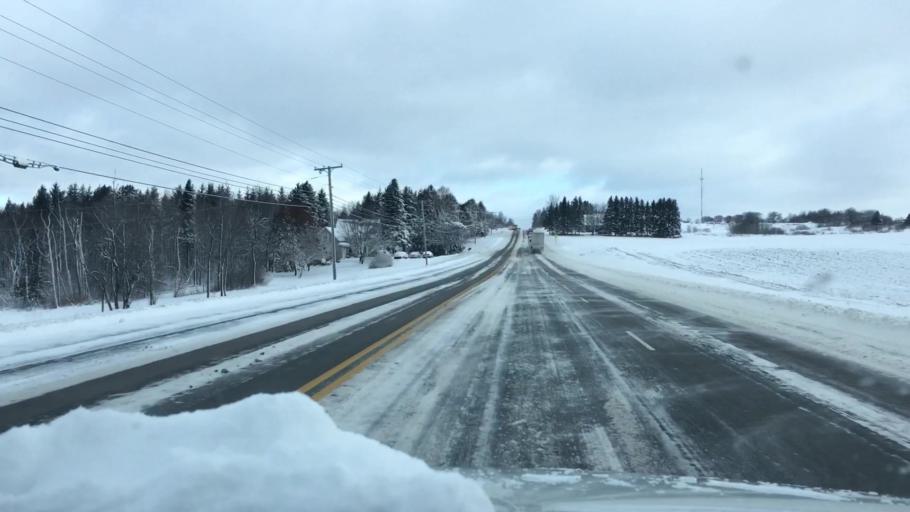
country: US
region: Maine
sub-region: Aroostook County
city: Presque Isle
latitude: 46.7207
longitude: -68.0066
